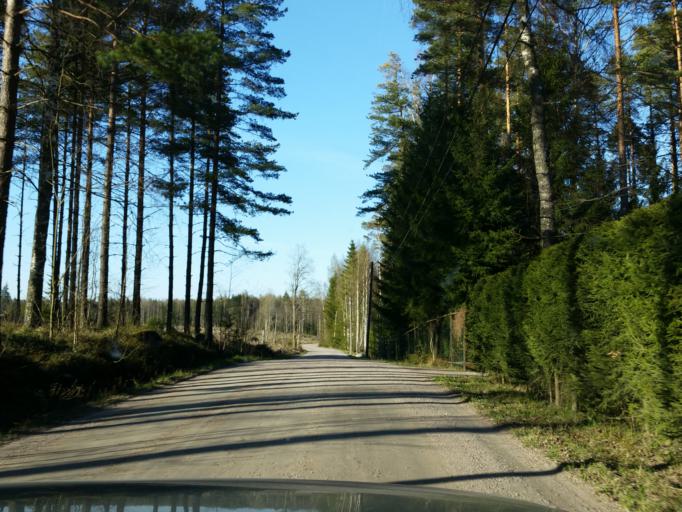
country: FI
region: Uusimaa
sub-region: Helsinki
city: Espoo
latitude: 60.1024
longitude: 24.5935
